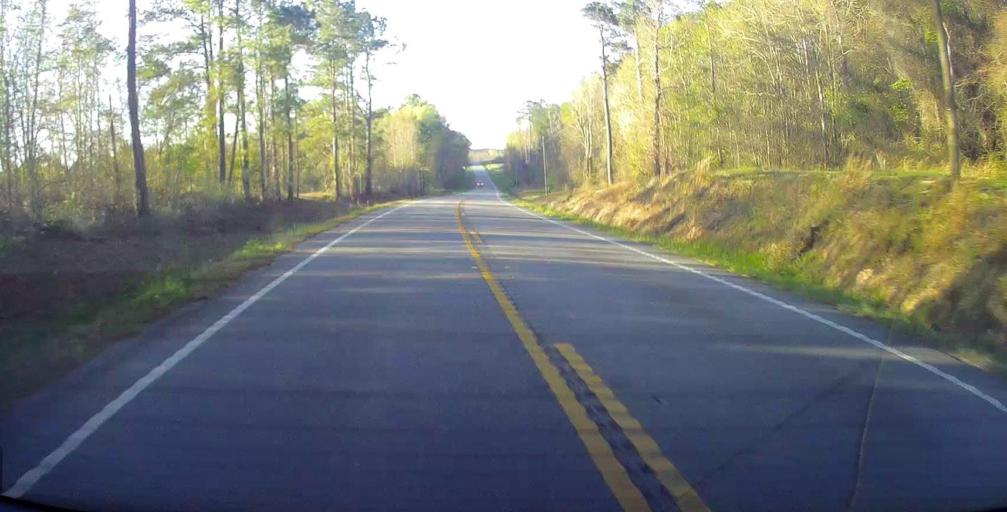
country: US
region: Georgia
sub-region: Wilcox County
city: Abbeville
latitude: 32.0401
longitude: -83.2572
